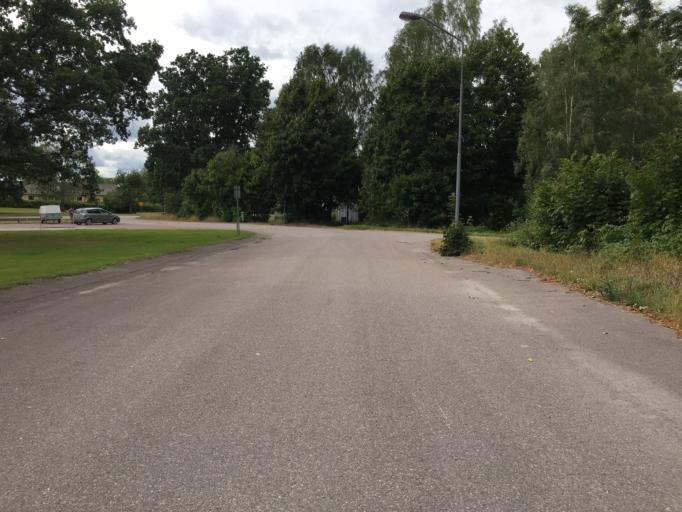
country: SE
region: Kalmar
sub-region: Nybro Kommun
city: Nybro
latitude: 56.9430
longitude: 15.9155
